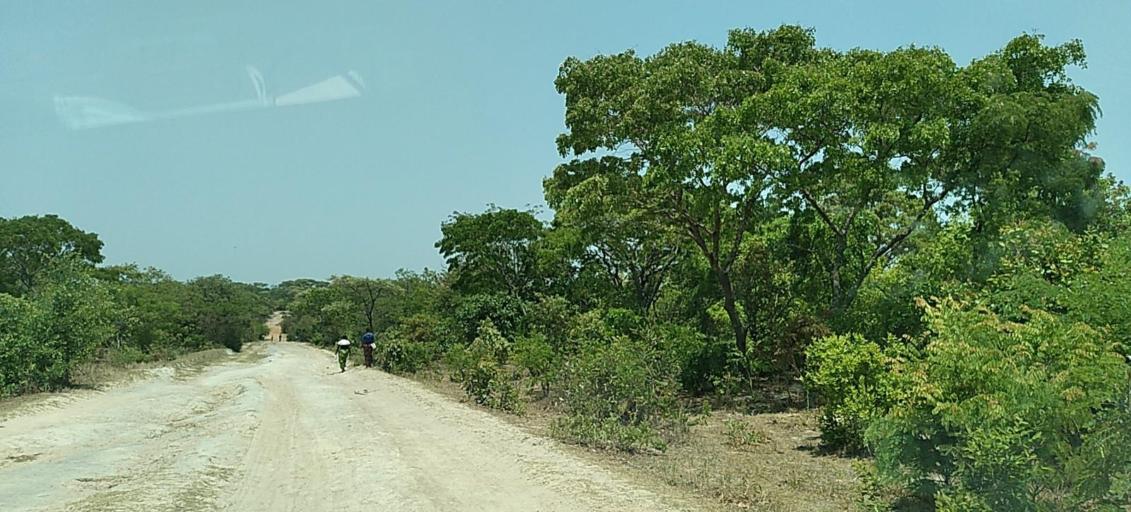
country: ZM
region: Copperbelt
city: Mpongwe
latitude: -13.8671
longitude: 27.8860
